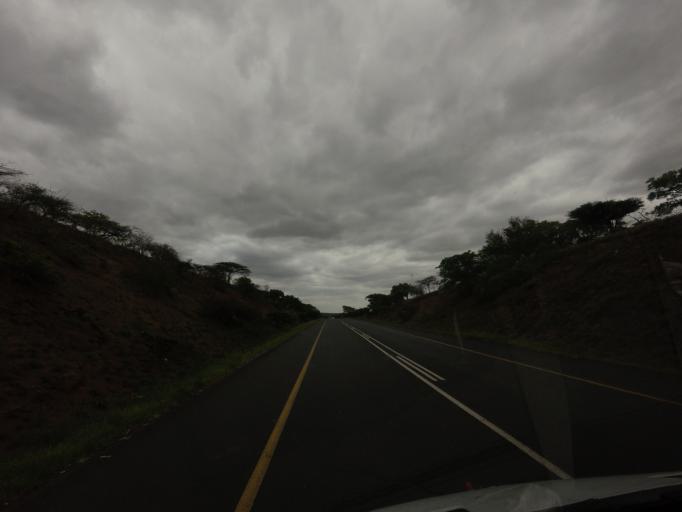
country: ZA
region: KwaZulu-Natal
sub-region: uMkhanyakude District Municipality
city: Hluhluwe
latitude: -27.9017
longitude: 32.1992
